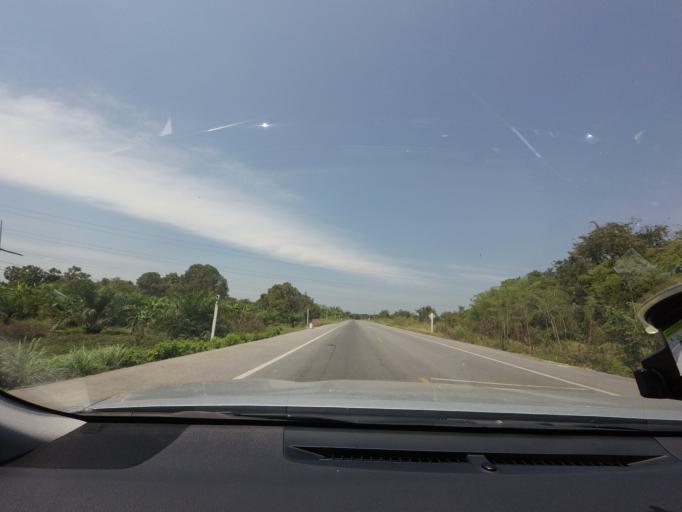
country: TH
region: Surat Thani
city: Tha Chang
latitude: 9.2152
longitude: 99.1885
